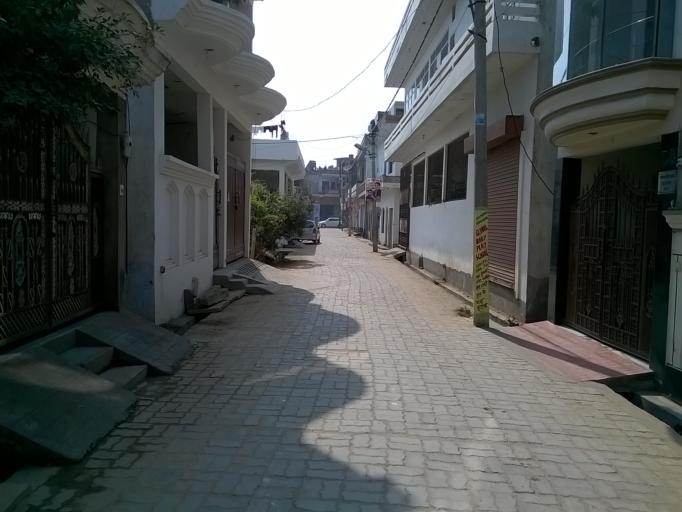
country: IN
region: Uttar Pradesh
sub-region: Etawah
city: Etawah
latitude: 26.7896
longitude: 79.0396
